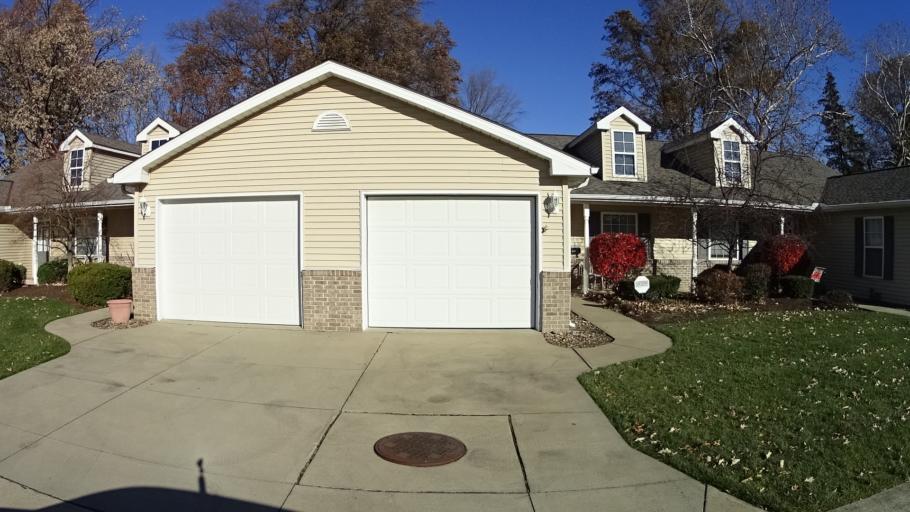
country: US
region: Ohio
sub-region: Lorain County
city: Elyria
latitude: 41.3832
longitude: -82.0785
